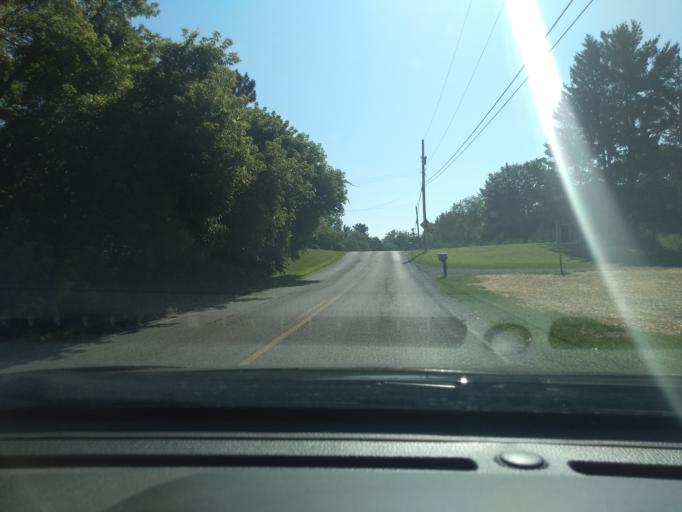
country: US
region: New York
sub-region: Erie County
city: Orchard Park
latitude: 42.7896
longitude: -78.6928
